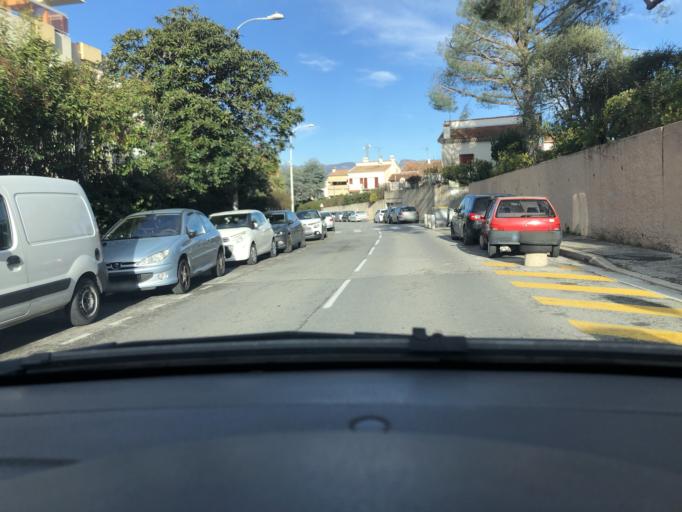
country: FR
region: Provence-Alpes-Cote d'Azur
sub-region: Departement des Alpes-Maritimes
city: Saint-Laurent-du-Var
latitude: 43.6794
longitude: 7.2104
